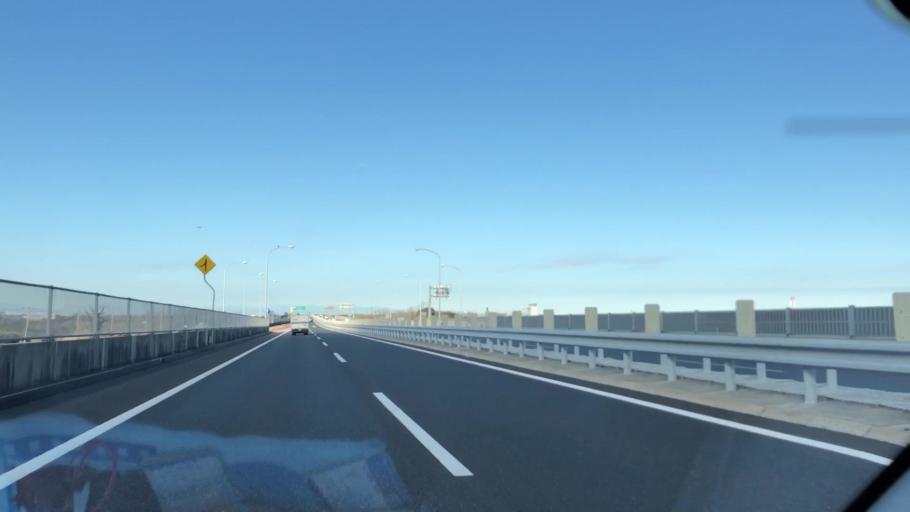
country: JP
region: Chiba
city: Kisarazu
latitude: 35.4150
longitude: 139.9510
